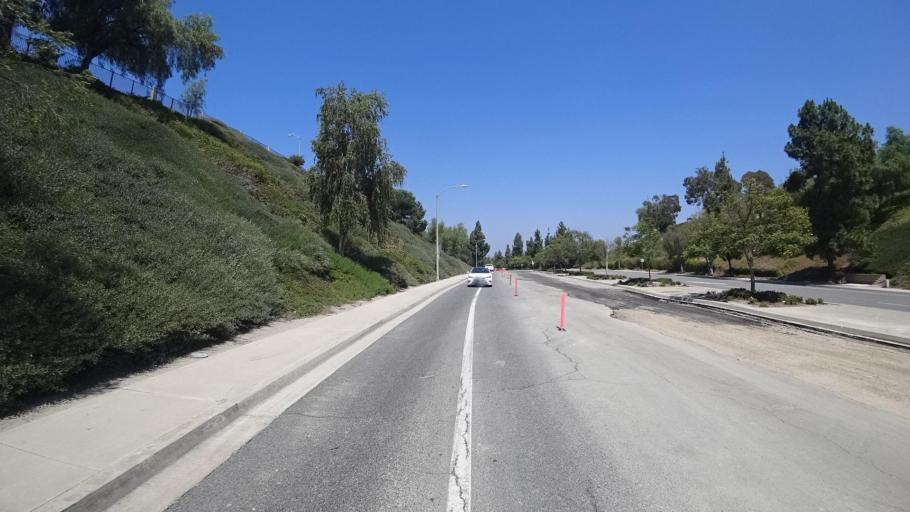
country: US
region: California
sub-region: San Diego County
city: Vista
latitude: 33.2261
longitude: -117.2638
